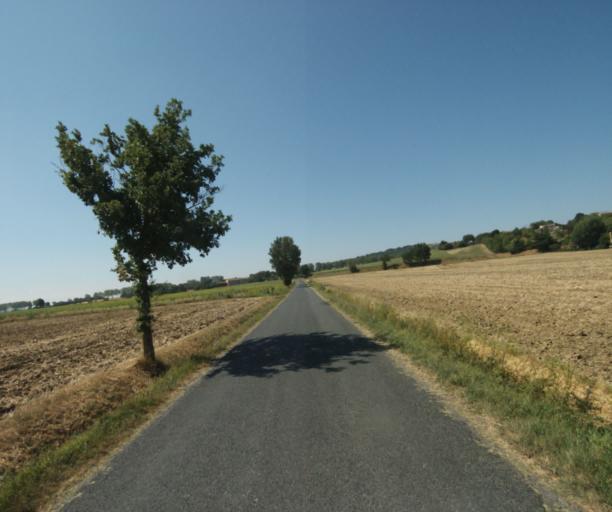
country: FR
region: Midi-Pyrenees
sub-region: Departement de la Haute-Garonne
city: Revel
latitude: 43.5112
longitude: 1.9533
